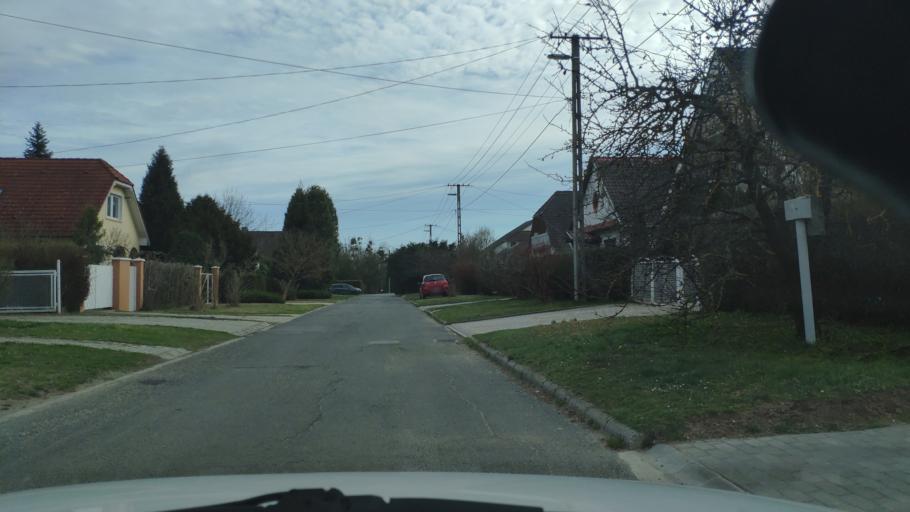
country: HU
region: Zala
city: Nagykanizsa
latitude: 46.4828
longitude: 16.9904
